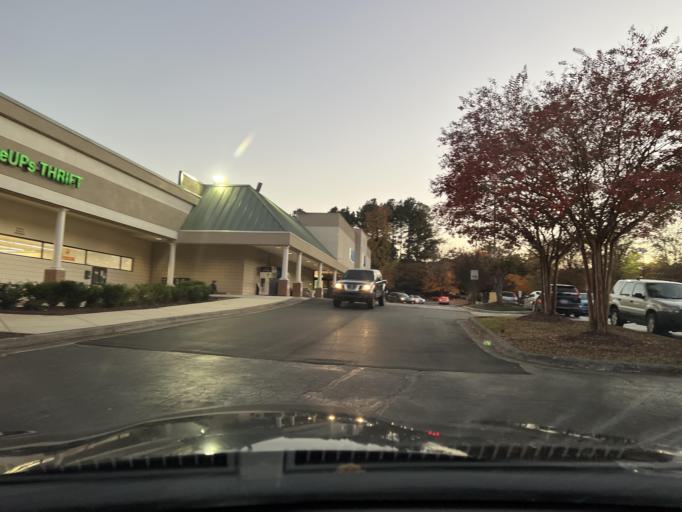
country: US
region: North Carolina
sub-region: Wake County
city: West Raleigh
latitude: 35.8922
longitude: -78.5998
